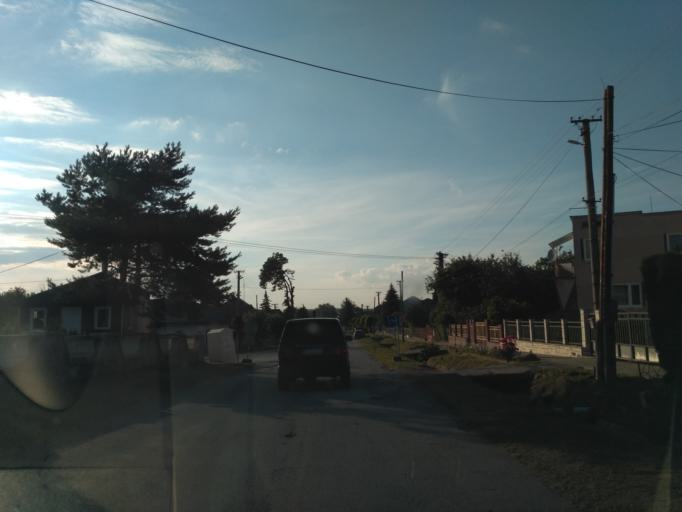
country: SK
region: Kosicky
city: Kosice
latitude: 48.7342
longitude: 21.4407
